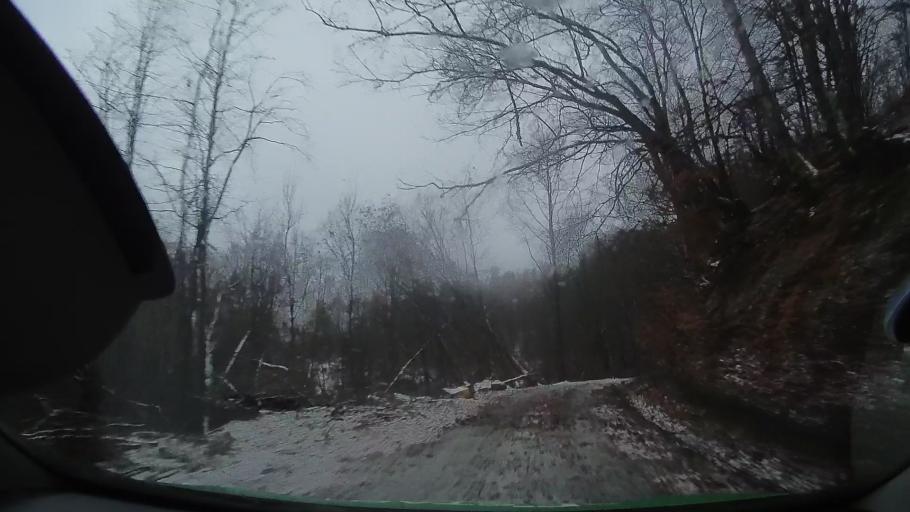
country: RO
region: Alba
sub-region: Comuna Avram Iancu
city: Avram Iancu
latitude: 46.3024
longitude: 22.7935
